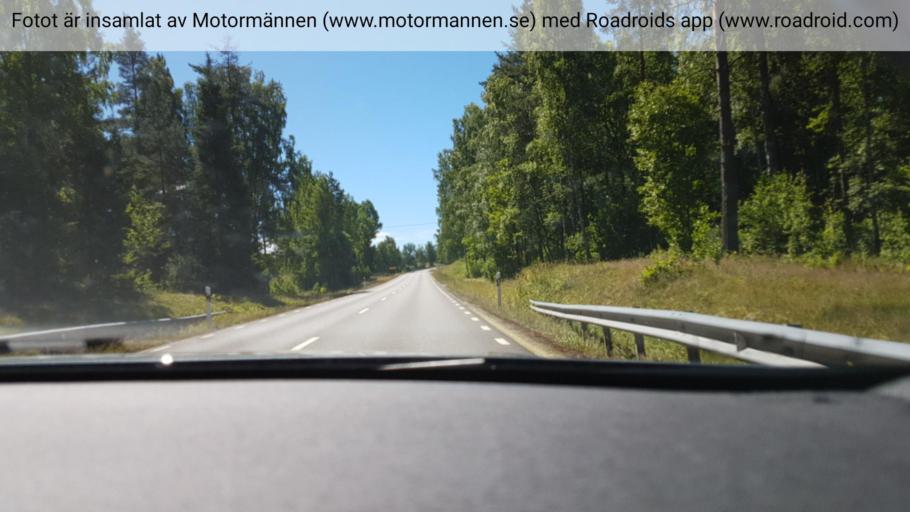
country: SE
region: Joenkoeping
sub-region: Mullsjo Kommun
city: Mullsjoe
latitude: 57.8608
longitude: 13.8576
